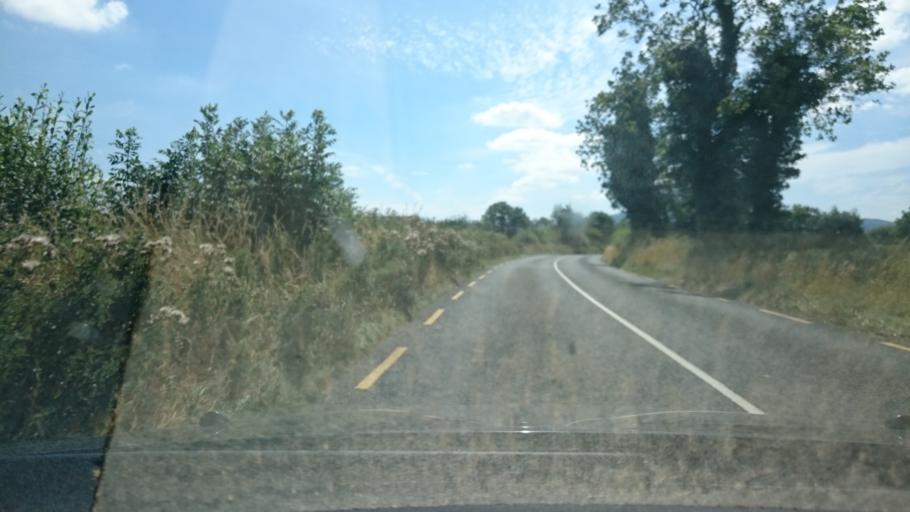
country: IE
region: Leinster
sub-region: Kilkenny
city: Graiguenamanagh
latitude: 52.5625
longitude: -6.9521
